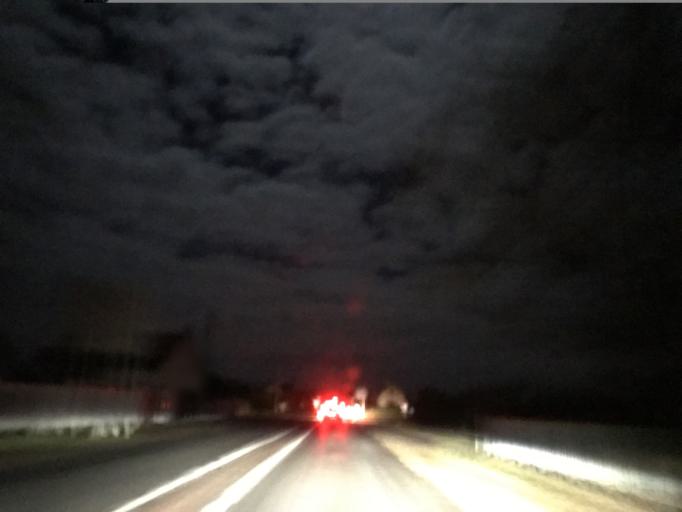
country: FR
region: Auvergne
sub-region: Departement de l'Allier
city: Hauterive
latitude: 46.0775
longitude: 3.4413
